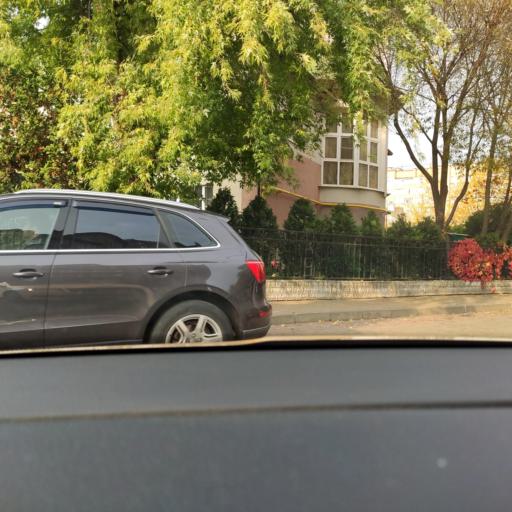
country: RU
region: Moskovskaya
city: Ivanteyevka
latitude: 55.9660
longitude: 37.9116
